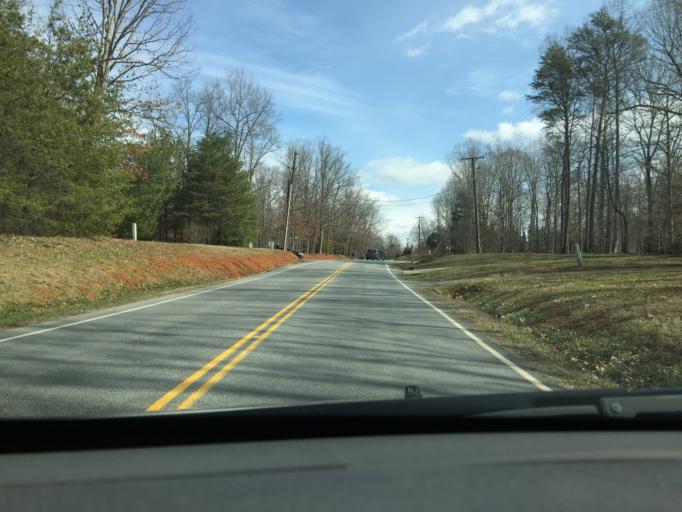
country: US
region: Virginia
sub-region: Bedford County
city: Forest
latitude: 37.3247
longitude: -79.3059
